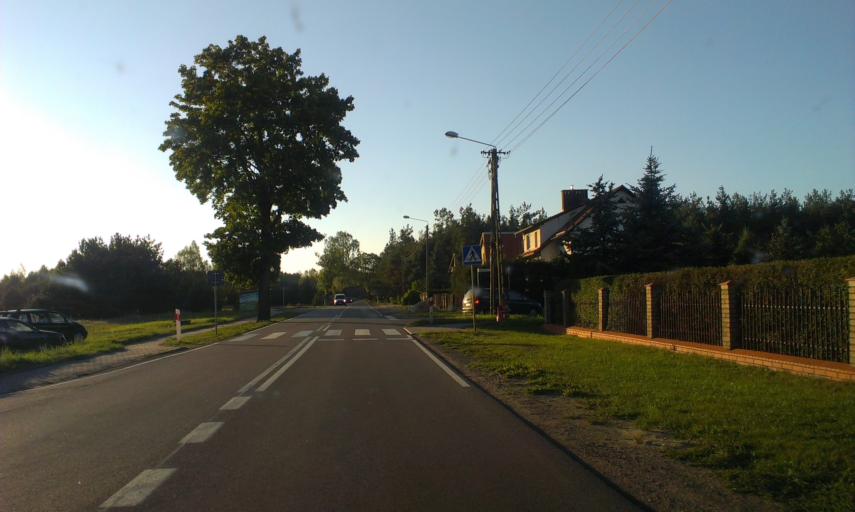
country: PL
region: Pomeranian Voivodeship
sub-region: Powiat czluchowski
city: Czarne
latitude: 53.6884
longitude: 16.9282
